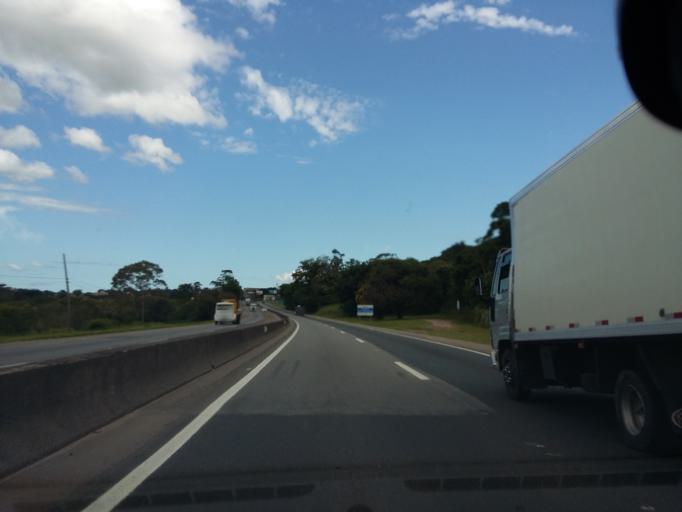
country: BR
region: Santa Catarina
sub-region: Tijucas
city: Tijucas
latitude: -27.3673
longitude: -48.6341
